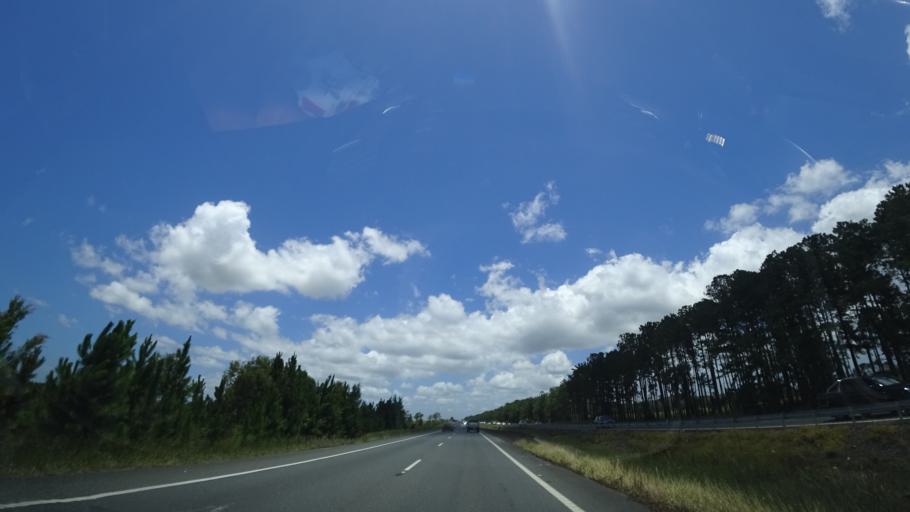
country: AU
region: Queensland
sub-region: Sunshine Coast
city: Little Mountain
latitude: -26.8109
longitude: 153.0390
